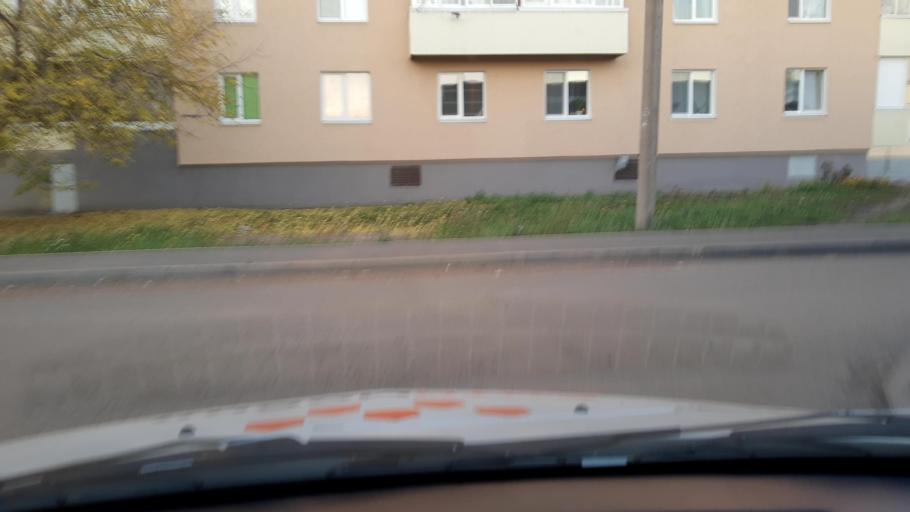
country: RU
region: Bashkortostan
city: Iglino
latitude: 54.7553
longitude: 56.2478
